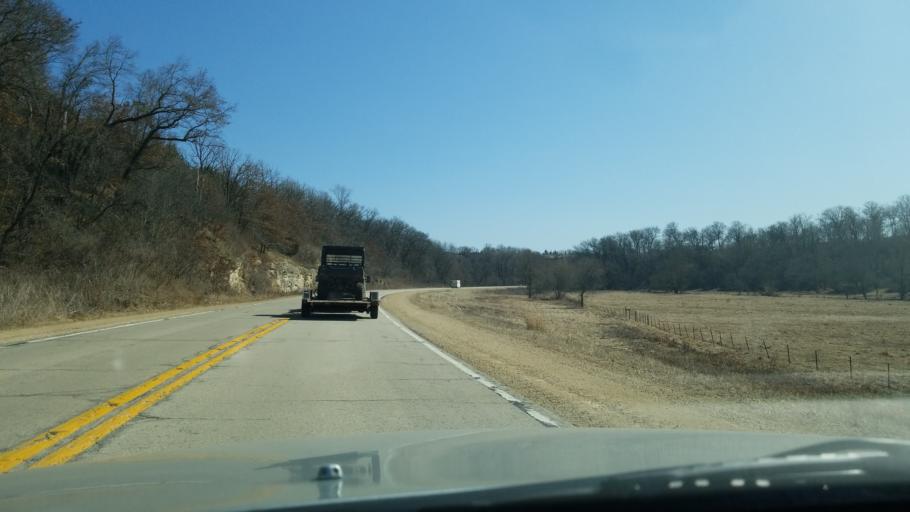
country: US
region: Wisconsin
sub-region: Iowa County
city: Mineral Point
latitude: 42.8751
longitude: -90.2075
